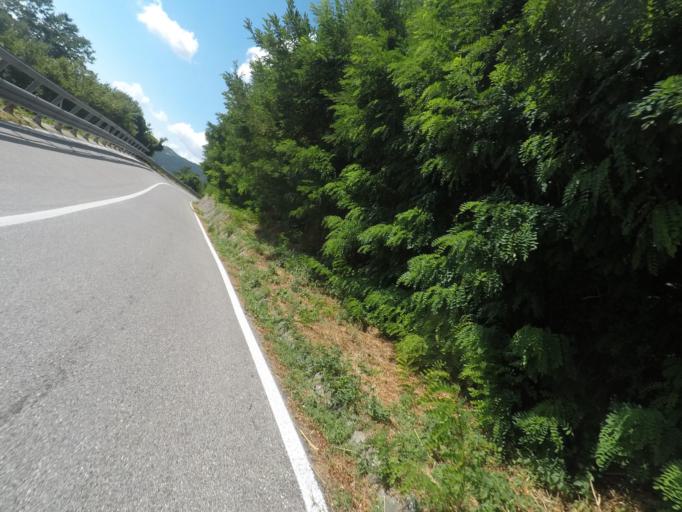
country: IT
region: Tuscany
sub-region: Provincia di Massa-Carrara
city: Comano
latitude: 44.2680
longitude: 10.1798
